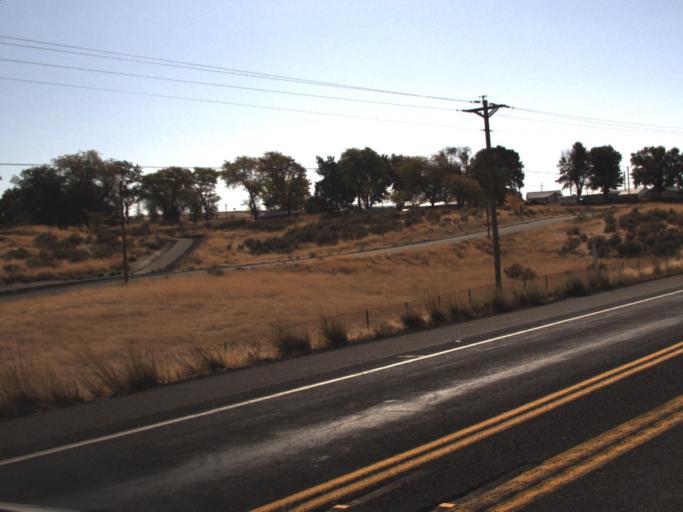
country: US
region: Washington
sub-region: Franklin County
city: Basin City
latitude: 46.5760
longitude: -119.0041
